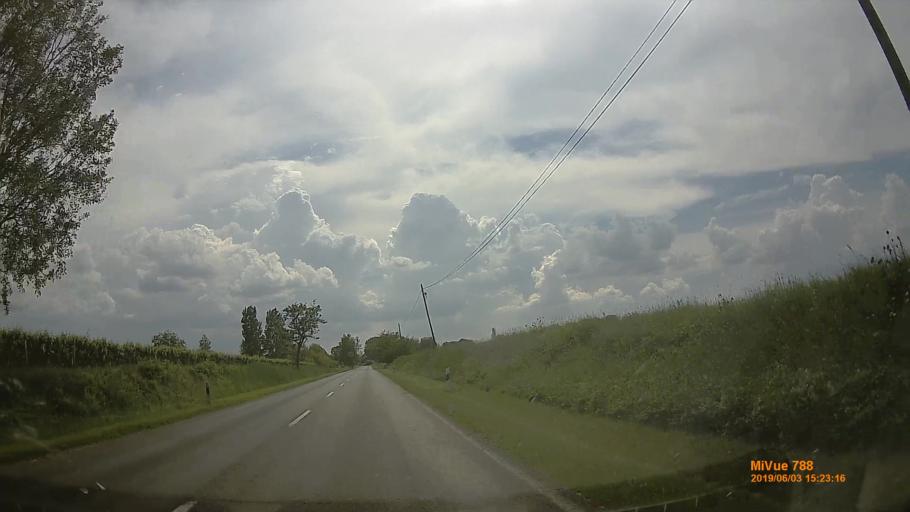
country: HU
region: Bacs-Kiskun
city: Tazlar
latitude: 46.6217
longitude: 19.4897
